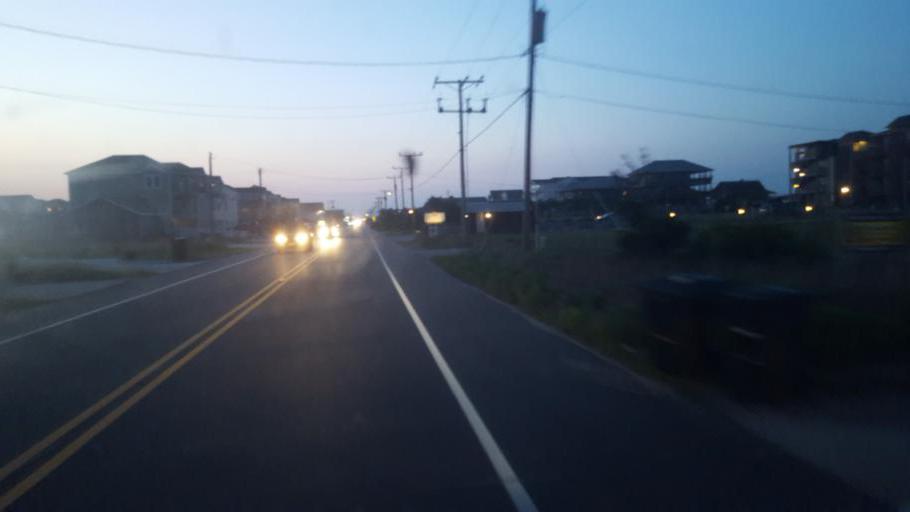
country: US
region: North Carolina
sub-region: Dare County
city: Kill Devil Hills
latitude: 36.0009
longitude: -75.6494
